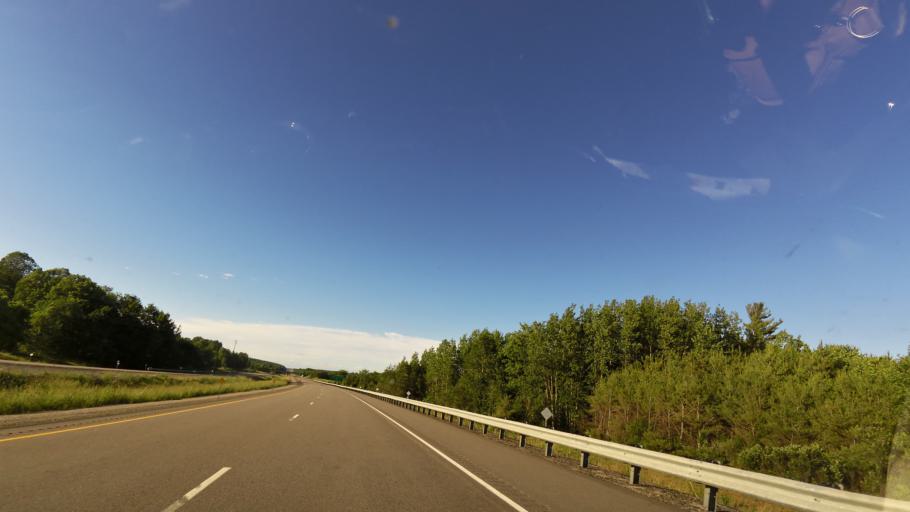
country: CA
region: Ontario
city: Barrie
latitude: 44.6156
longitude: -79.6638
